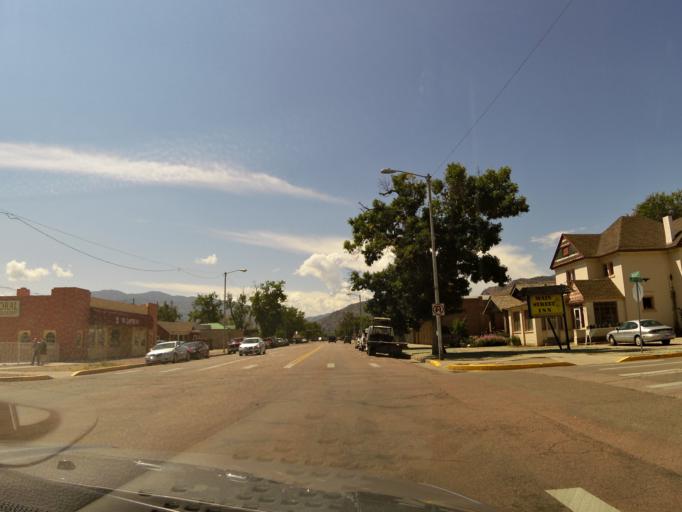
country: US
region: Colorado
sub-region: Fremont County
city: Canon City
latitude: 38.4443
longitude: -105.2328
